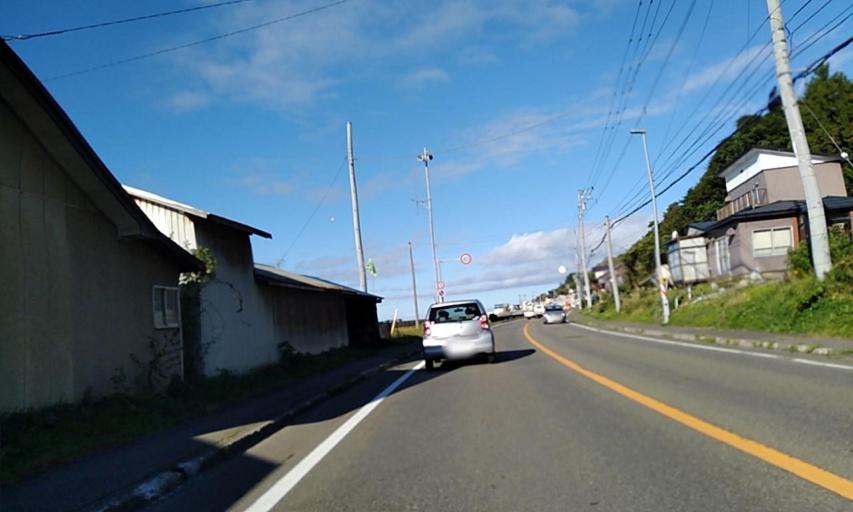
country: JP
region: Hokkaido
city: Shizunai-furukawacho
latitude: 42.1767
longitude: 142.7447
